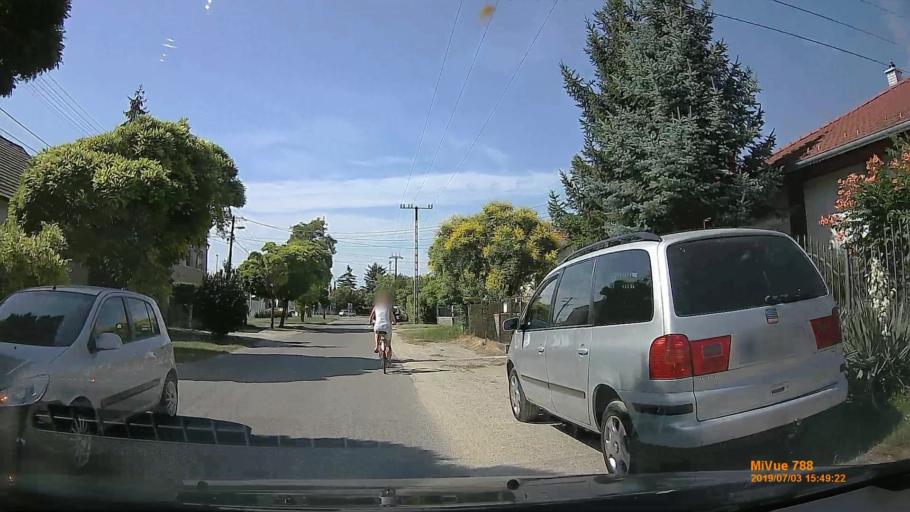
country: HU
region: Gyor-Moson-Sopron
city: Toltestava
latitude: 47.6973
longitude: 17.7340
